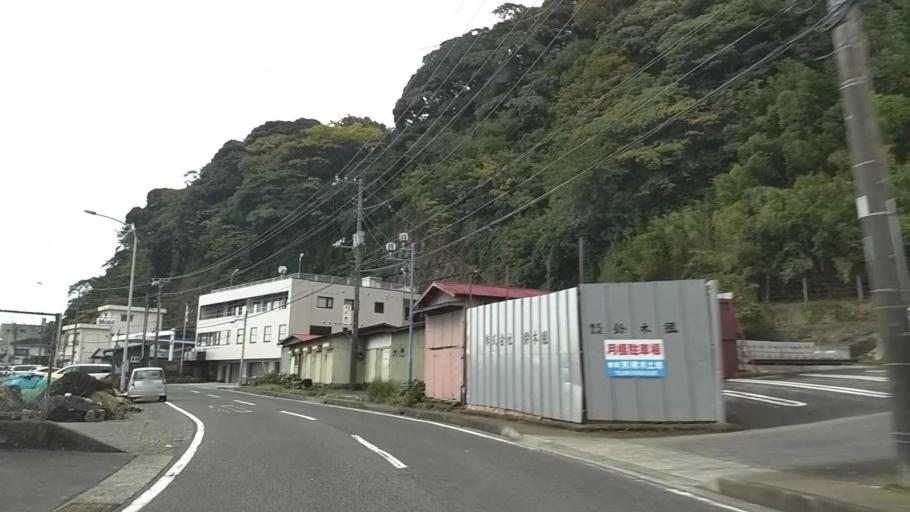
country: JP
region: Kanagawa
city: Yugawara
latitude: 35.1519
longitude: 139.1413
